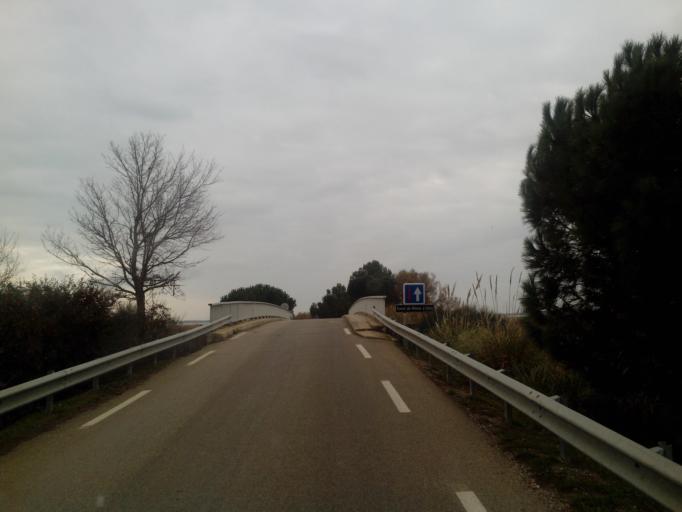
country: FR
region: Languedoc-Roussillon
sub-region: Departement du Gard
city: Vauvert
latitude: 43.6382
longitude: 4.2983
